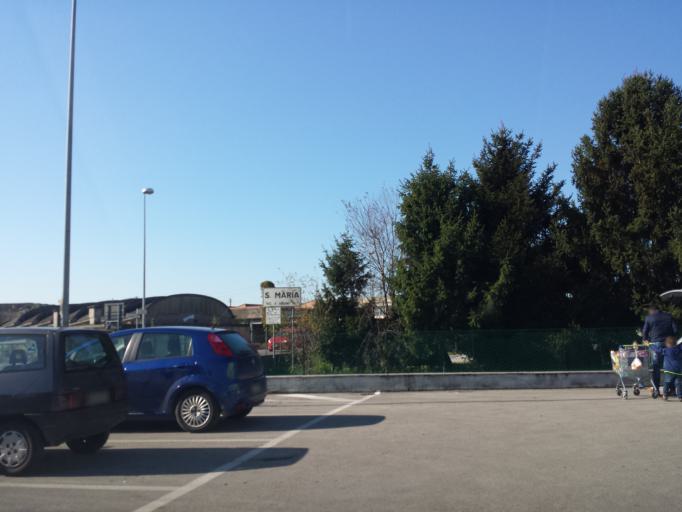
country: IT
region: Veneto
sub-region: Provincia di Vicenza
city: Camisano Vicentino
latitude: 45.5166
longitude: 11.7036
